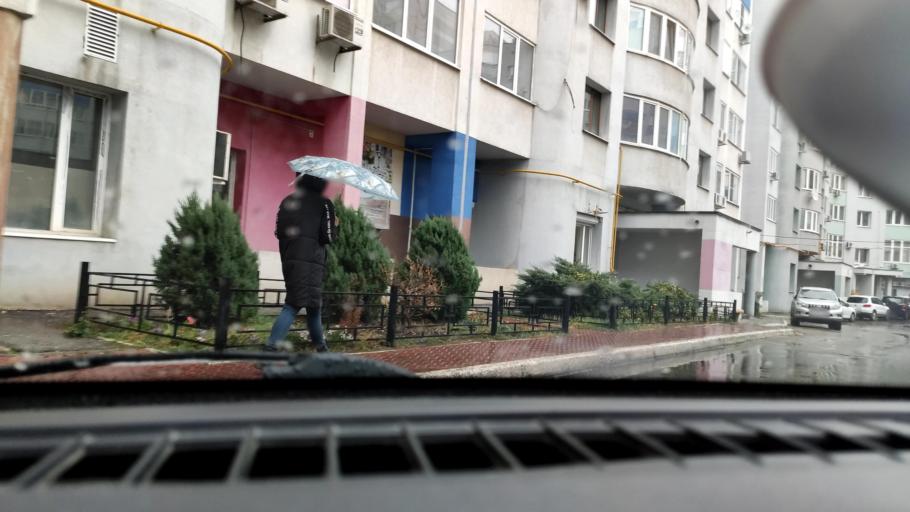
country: RU
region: Samara
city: Samara
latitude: 53.2236
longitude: 50.1749
